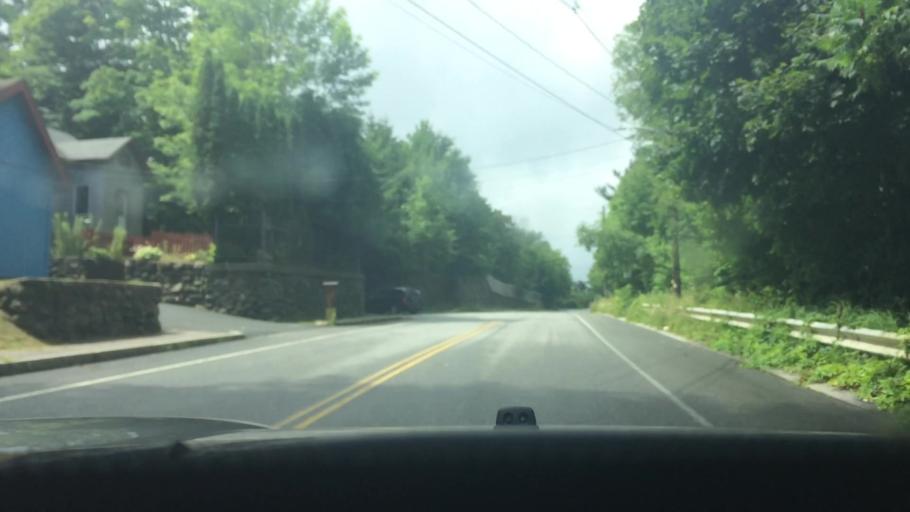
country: US
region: Massachusetts
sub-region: Worcester County
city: Templeton
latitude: 42.5641
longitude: -72.0342
